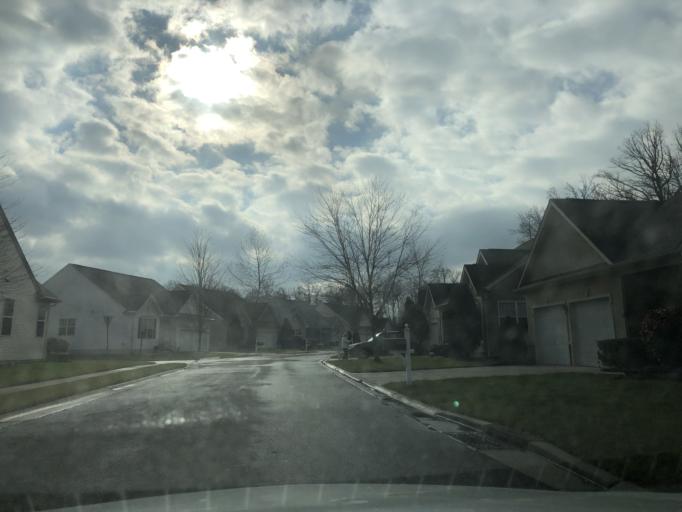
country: US
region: New Jersey
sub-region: Camden County
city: Bellmawr
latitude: 39.8439
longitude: -75.1008
